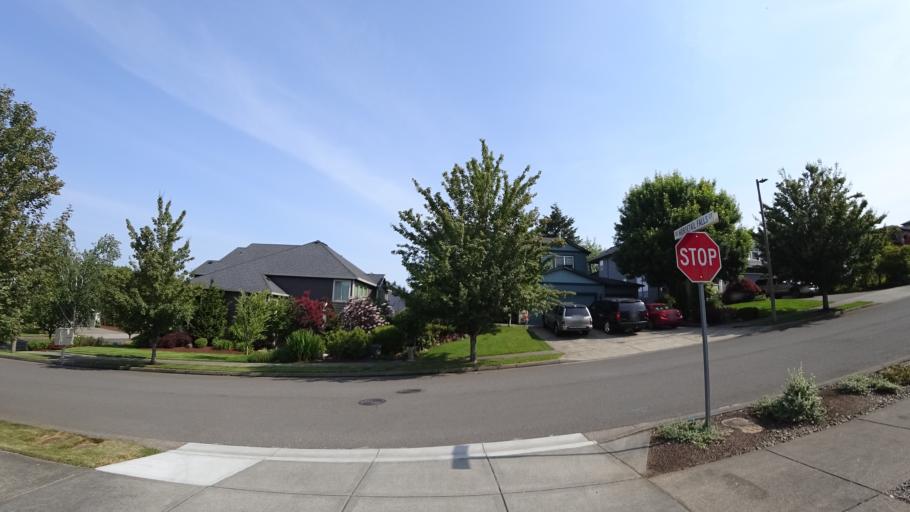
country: US
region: Oregon
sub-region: Clackamas County
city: Happy Valley
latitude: 45.4599
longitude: -122.5241
